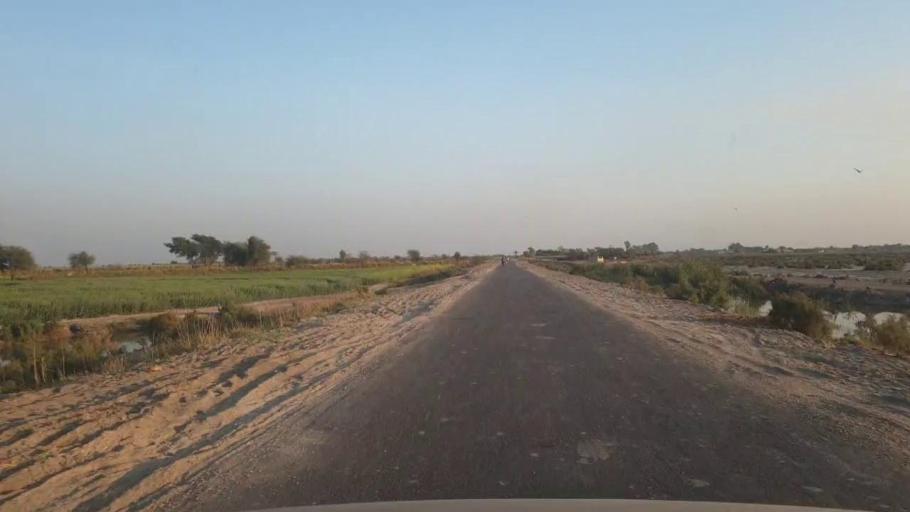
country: PK
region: Sindh
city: Chambar
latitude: 25.2843
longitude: 68.9101
